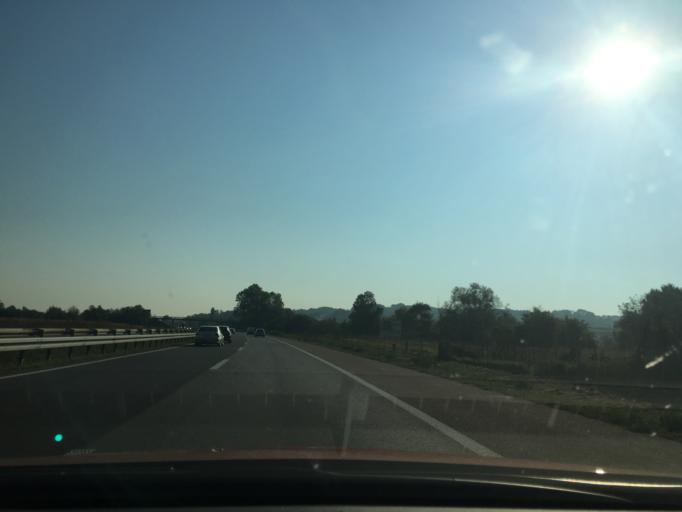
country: RS
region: Central Serbia
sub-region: Belgrade
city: Grocka
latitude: 44.5665
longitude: 20.6891
